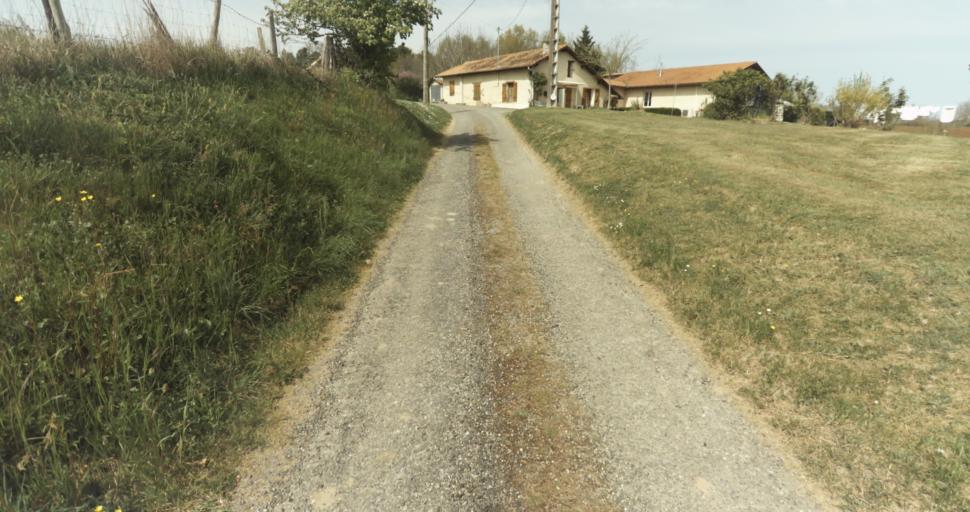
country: FR
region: Midi-Pyrenees
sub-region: Departement du Tarn-et-Garonne
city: Moissac
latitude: 44.1501
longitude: 1.1058
